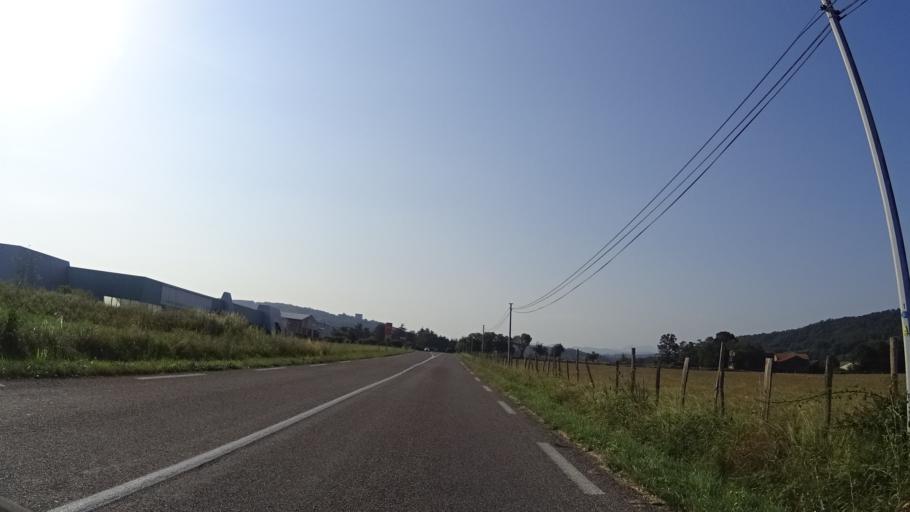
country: FR
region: Midi-Pyrenees
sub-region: Departement de l'Ariege
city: Mirepoix
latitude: 43.0487
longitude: 1.8913
